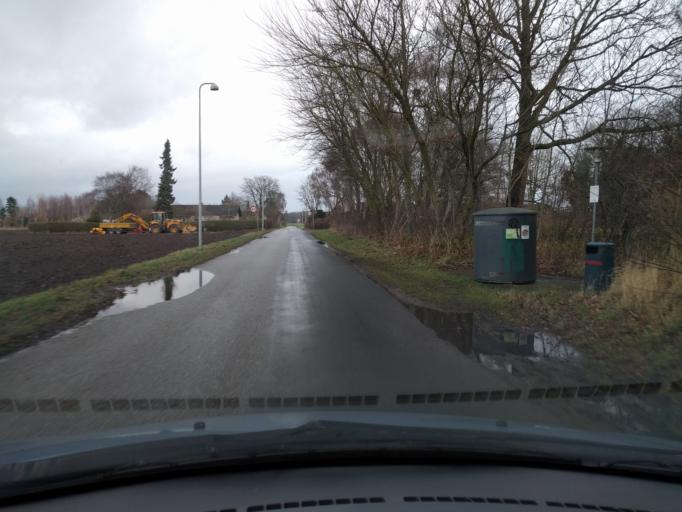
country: DK
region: South Denmark
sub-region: Kerteminde Kommune
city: Langeskov
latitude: 55.3415
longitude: 10.5435
